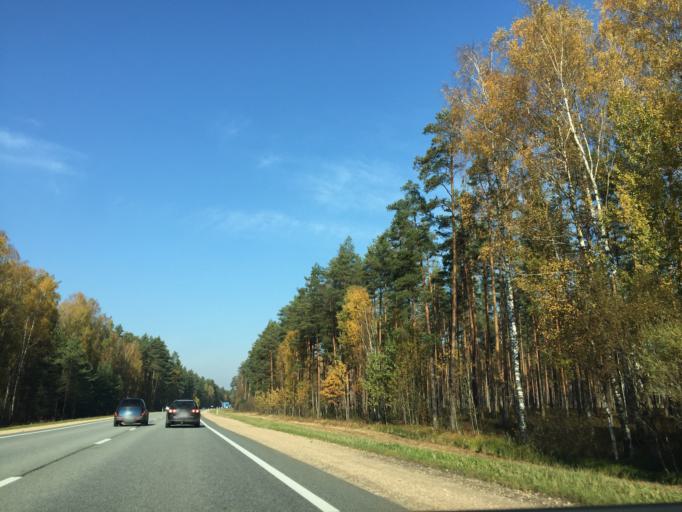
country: LV
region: Babite
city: Pinki
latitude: 56.9095
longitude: 23.9166
